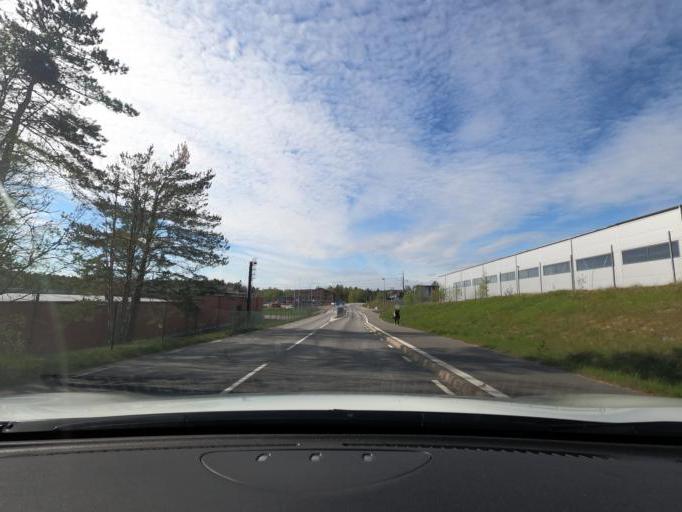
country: SE
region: Vaestra Goetaland
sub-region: Harryda Kommun
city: Landvetter
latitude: 57.6760
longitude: 12.2428
